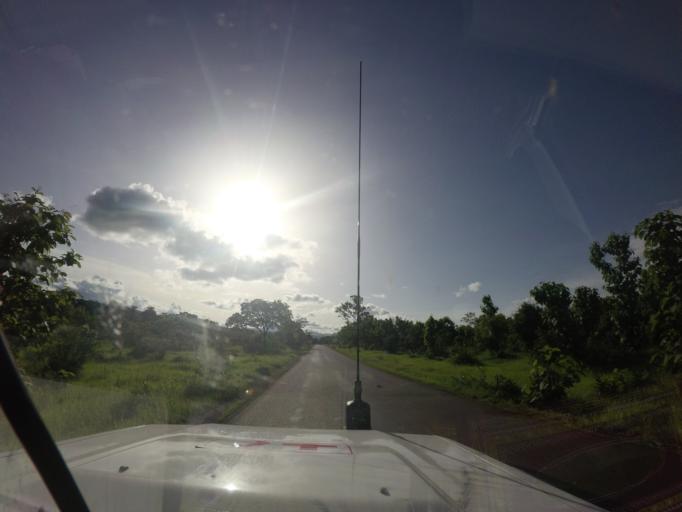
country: GN
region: Kindia
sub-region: Kindia
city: Kindia
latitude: 9.9935
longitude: -12.7506
